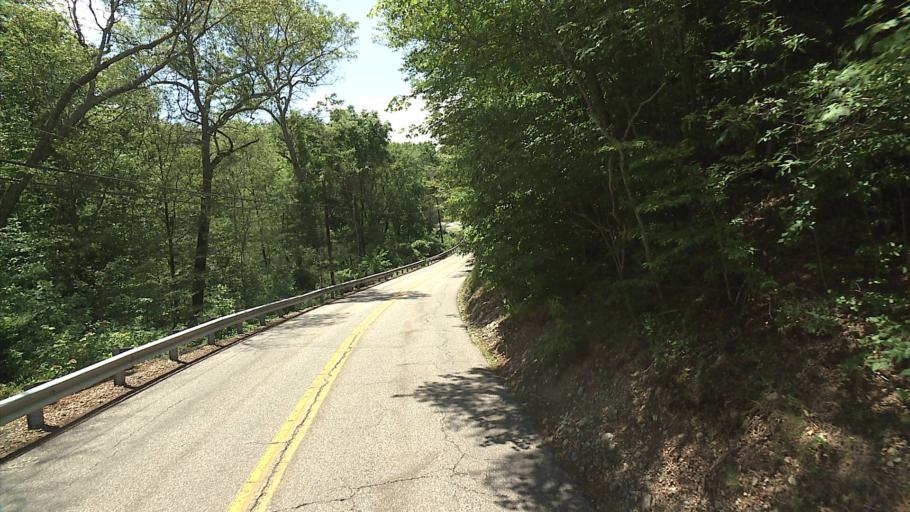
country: US
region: Connecticut
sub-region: New London County
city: Preston City
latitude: 41.5203
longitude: -71.8879
